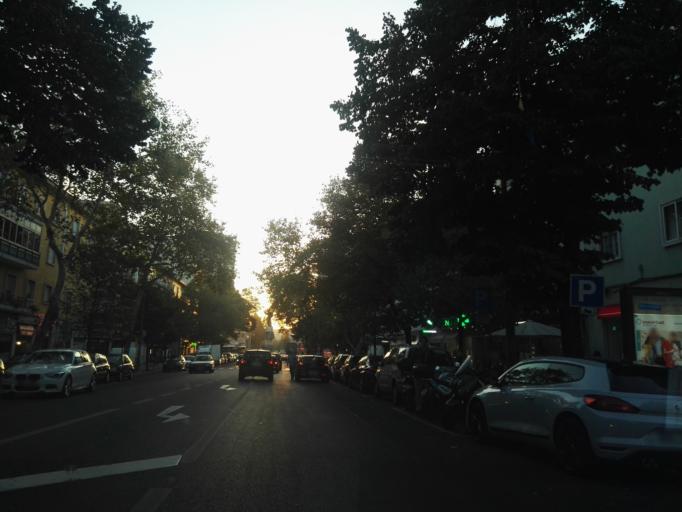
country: PT
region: Lisbon
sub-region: Lisbon
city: Lisbon
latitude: 38.7537
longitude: -9.1422
